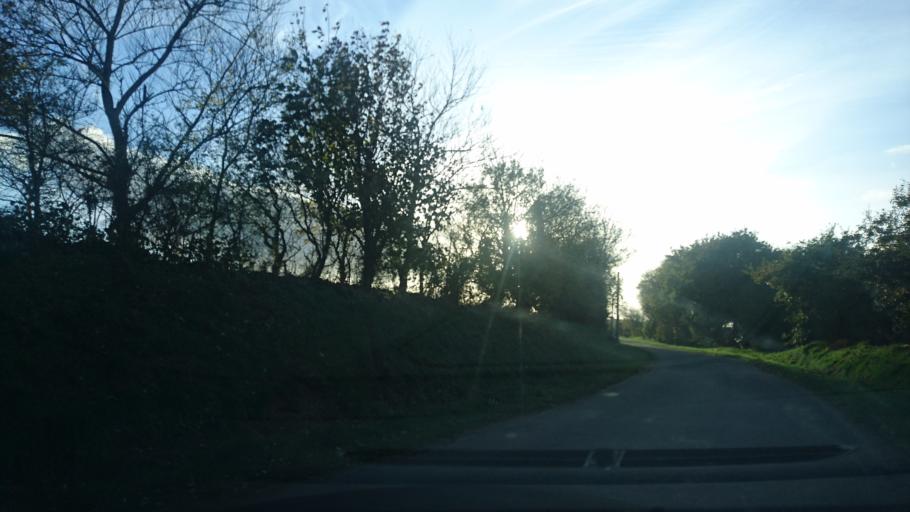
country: FR
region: Brittany
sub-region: Departement du Finistere
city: Lampaul-Plouarzel
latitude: 48.4363
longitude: -4.7588
